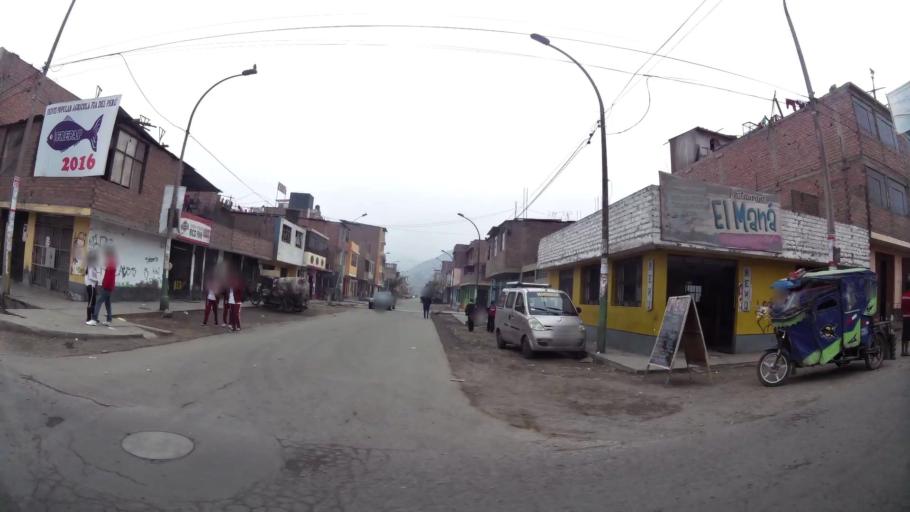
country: PE
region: Lima
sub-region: Lima
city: Independencia
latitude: -11.9438
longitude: -76.9763
